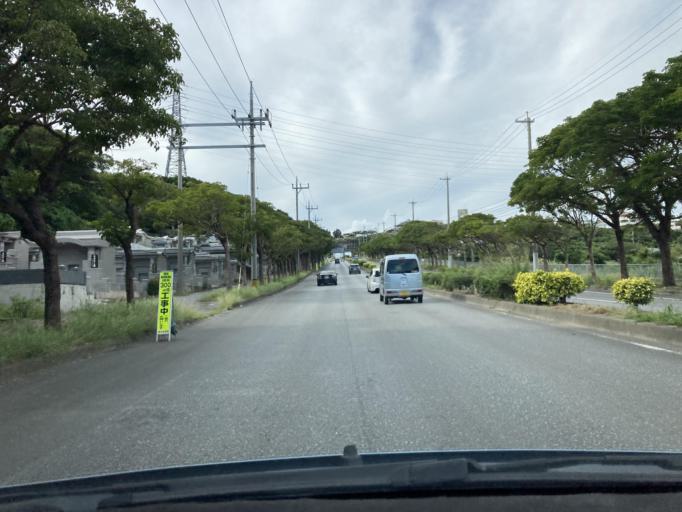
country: JP
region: Okinawa
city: Gushikawa
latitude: 26.3436
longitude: 127.8405
